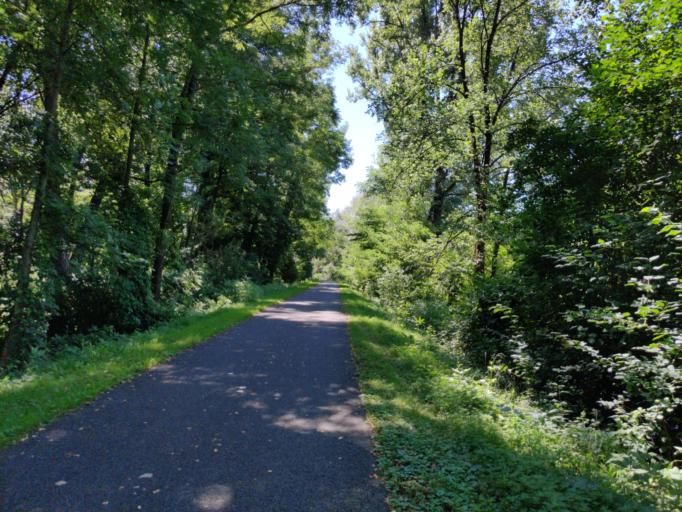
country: AT
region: Styria
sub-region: Politischer Bezirk Leibnitz
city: Retznei
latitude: 46.7326
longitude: 15.5782
